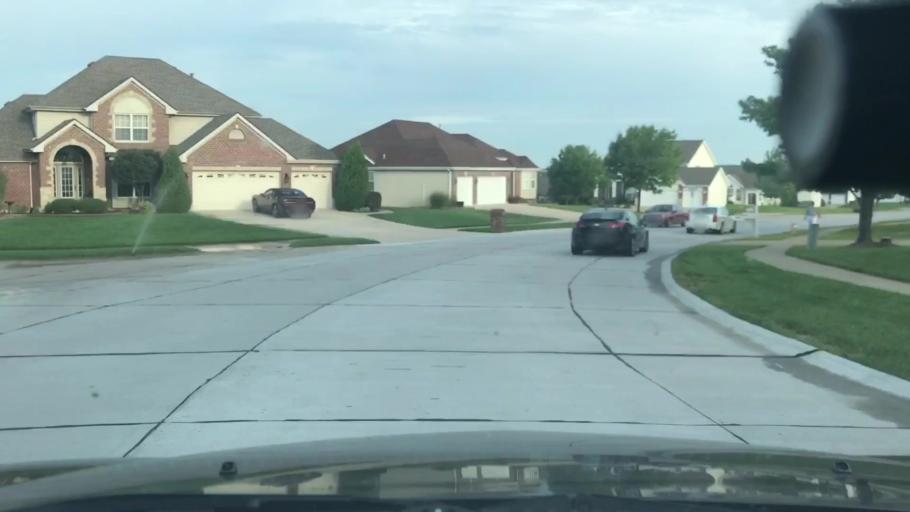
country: US
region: Missouri
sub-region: Saint Charles County
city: Wentzville
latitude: 38.8145
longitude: -90.8895
